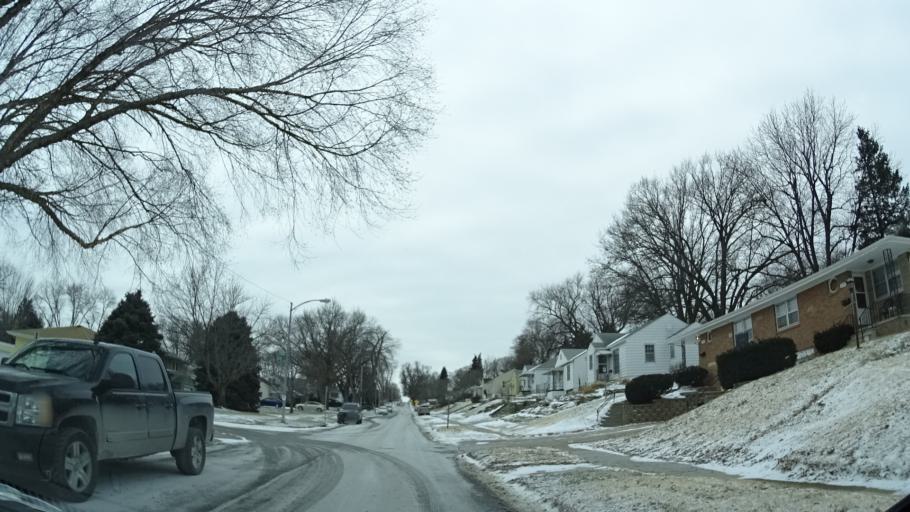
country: US
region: Nebraska
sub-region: Douglas County
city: Omaha
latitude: 41.2382
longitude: -95.9855
